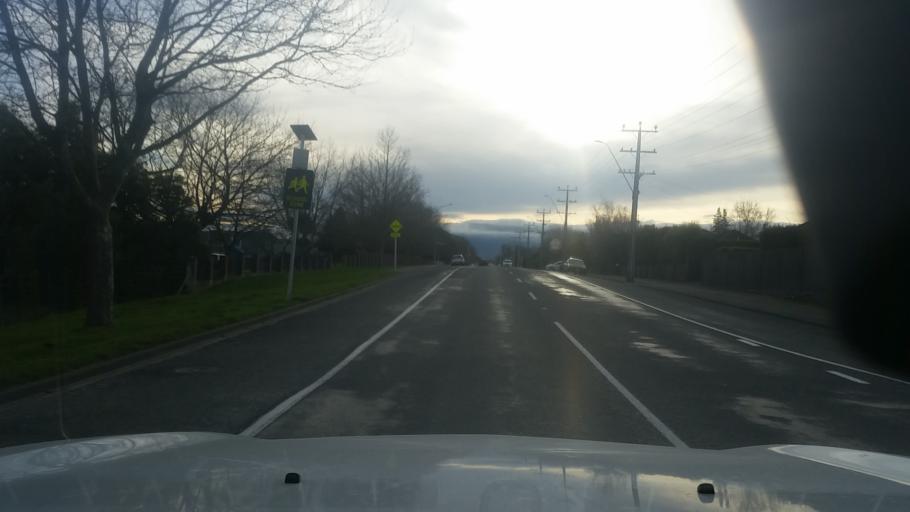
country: NZ
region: Wellington
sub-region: Masterton District
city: Masterton
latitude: -40.9480
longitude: 175.6804
